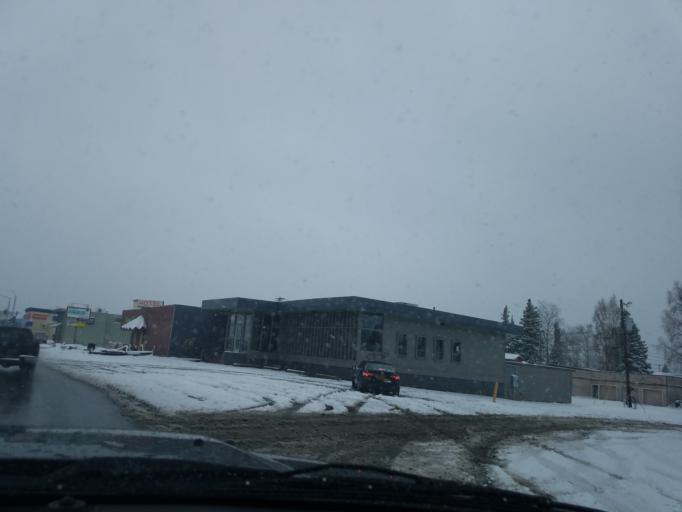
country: US
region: Alaska
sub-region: Anchorage Municipality
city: Anchorage
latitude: 61.1924
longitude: -149.9054
